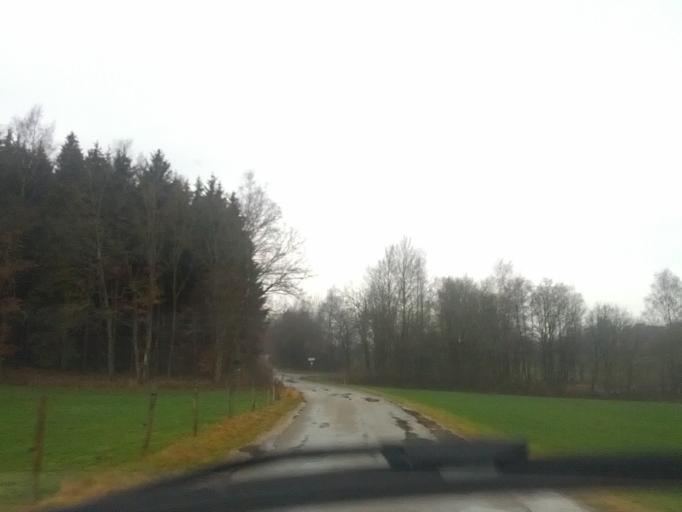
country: DE
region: Baden-Wuerttemberg
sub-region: Tuebingen Region
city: Rot an der Rot
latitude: 47.9894
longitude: 9.9972
